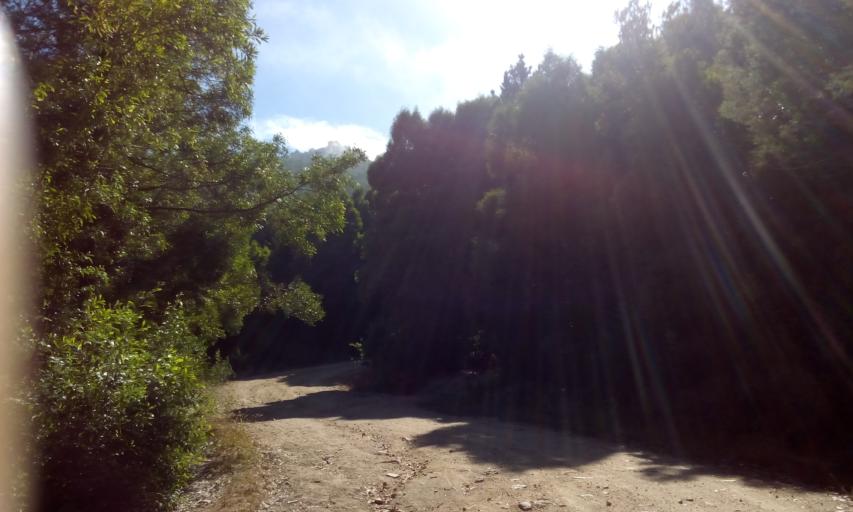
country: PT
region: Lisbon
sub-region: Sintra
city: Colares
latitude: 38.7772
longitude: -9.4348
